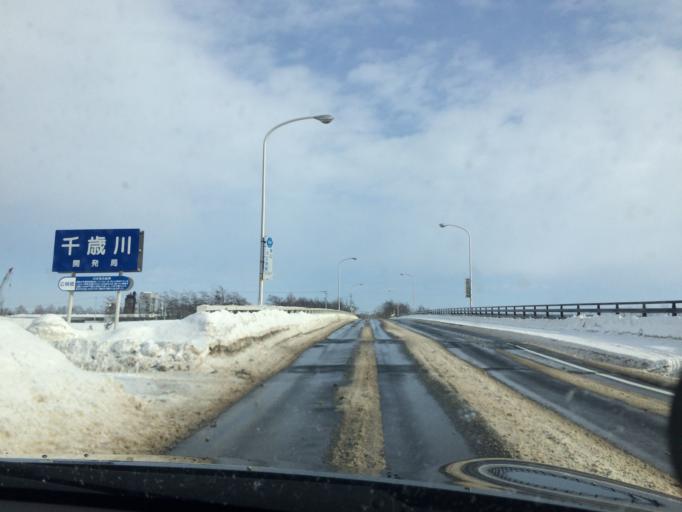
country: JP
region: Hokkaido
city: Kitahiroshima
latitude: 43.0175
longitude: 141.5782
